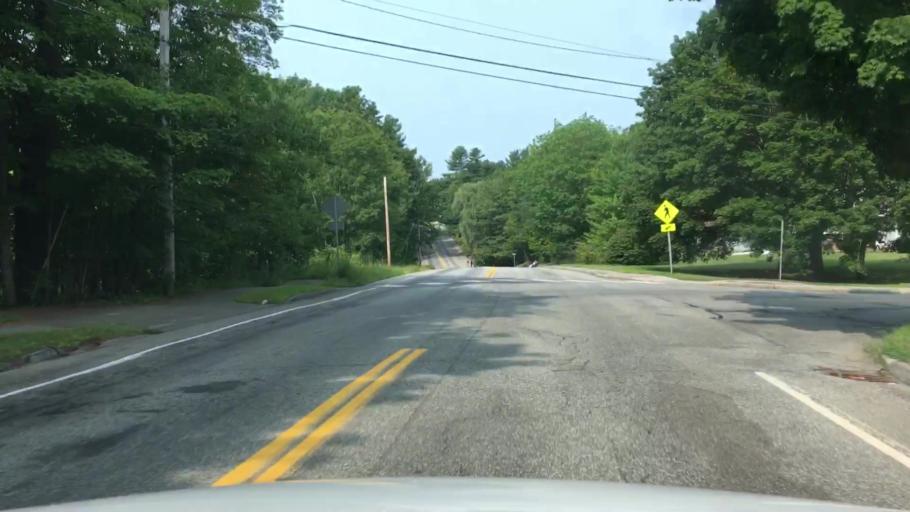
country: US
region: Maine
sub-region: Kennebec County
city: Augusta
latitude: 44.3198
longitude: -69.7496
